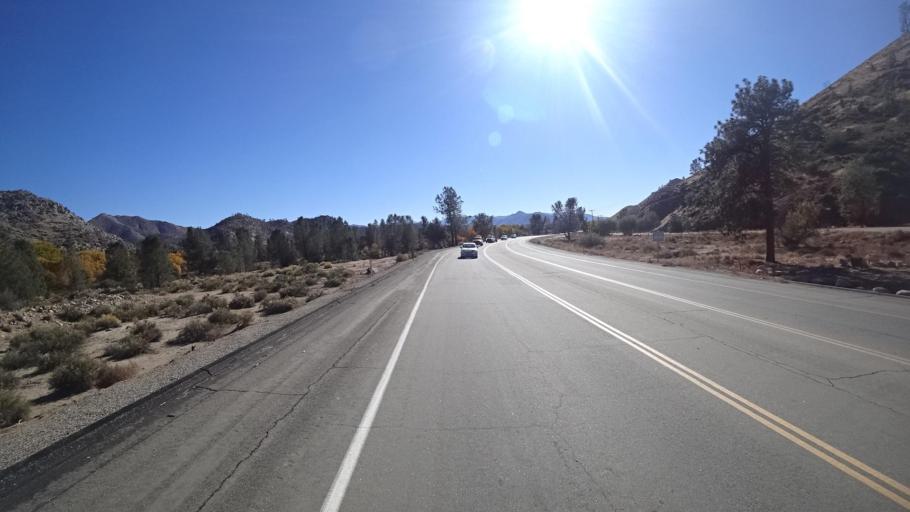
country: US
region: California
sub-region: Kern County
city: Kernville
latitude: 35.7480
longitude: -118.4220
